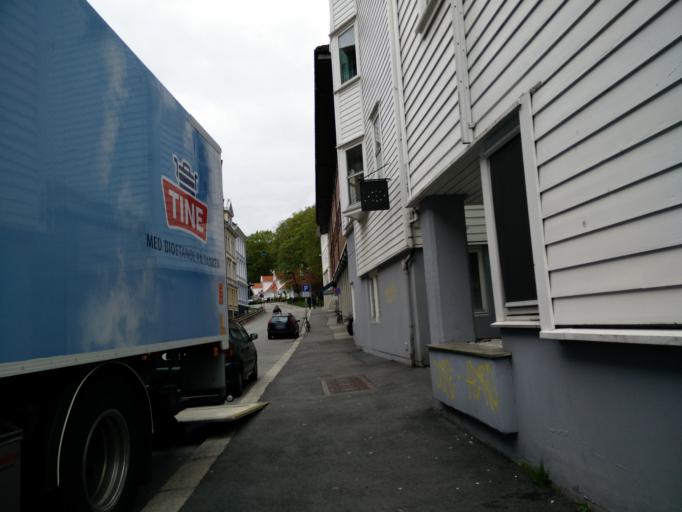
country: NO
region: Hordaland
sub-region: Bergen
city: Bergen
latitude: 60.3995
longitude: 5.3074
